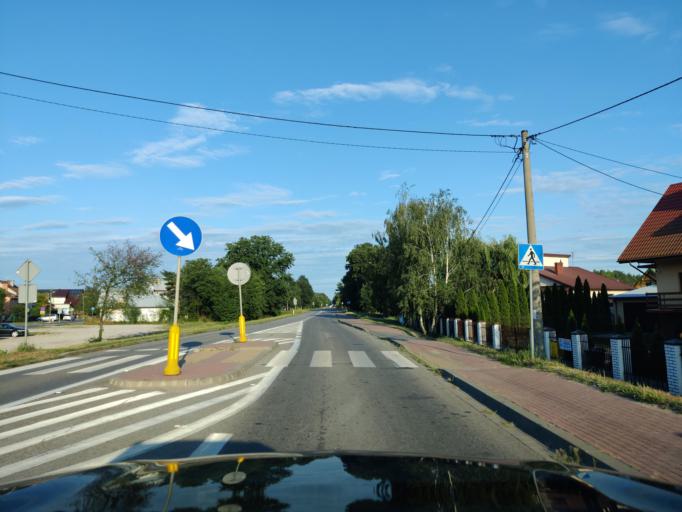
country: PL
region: Masovian Voivodeship
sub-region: Powiat pultuski
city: Pultusk
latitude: 52.6843
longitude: 21.1144
